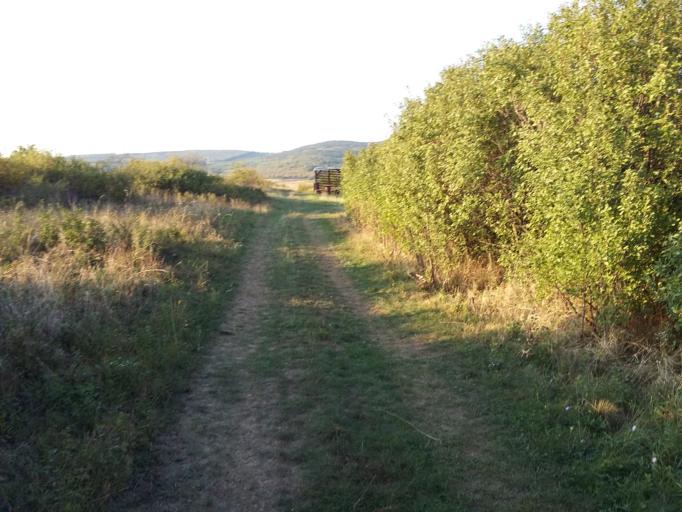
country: HU
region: Borsod-Abauj-Zemplen
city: Bekecs
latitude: 48.1597
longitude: 21.1729
